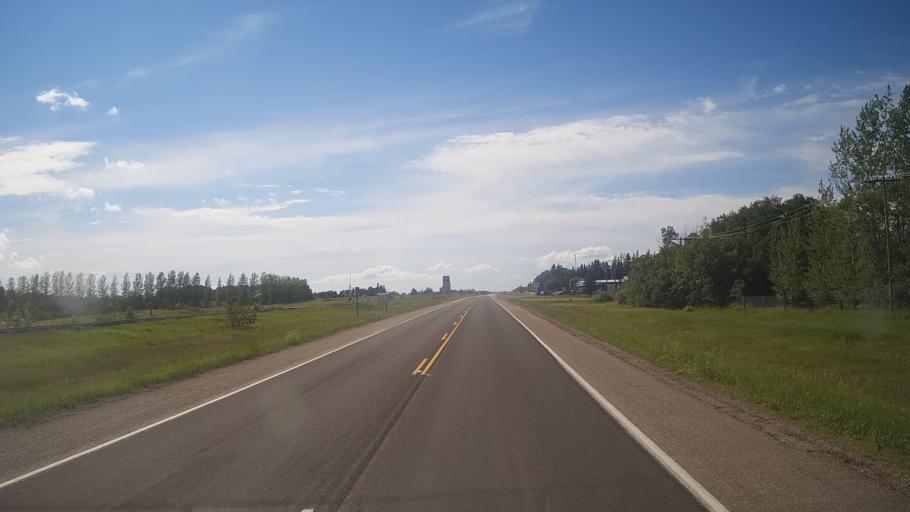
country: CA
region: Saskatchewan
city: Foam Lake
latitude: 51.2591
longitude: -103.7260
